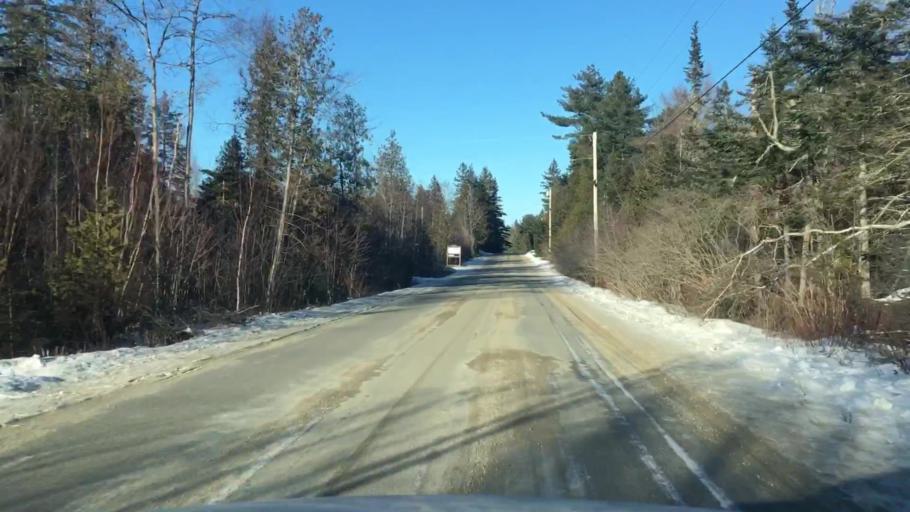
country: US
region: Maine
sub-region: Hancock County
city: Penobscot
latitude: 44.3918
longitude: -68.7146
